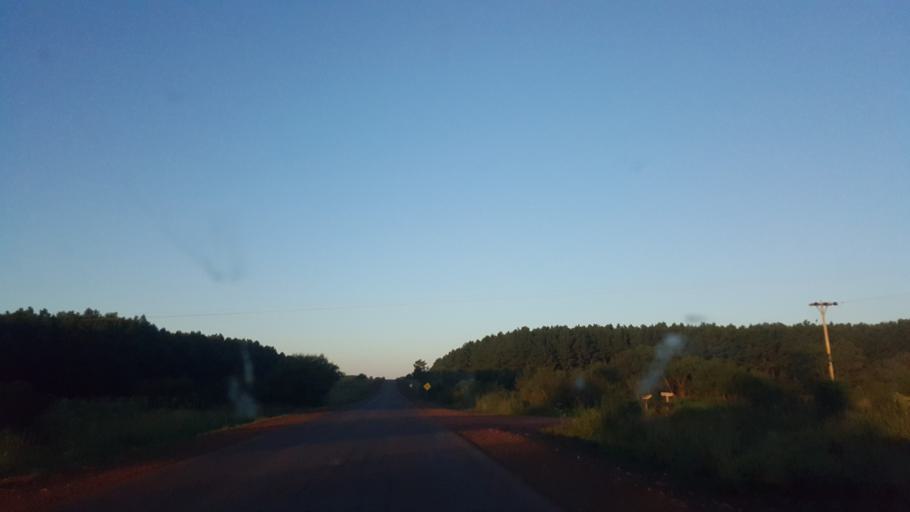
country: AR
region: Corrientes
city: Santo Tome
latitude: -28.4240
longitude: -55.9910
